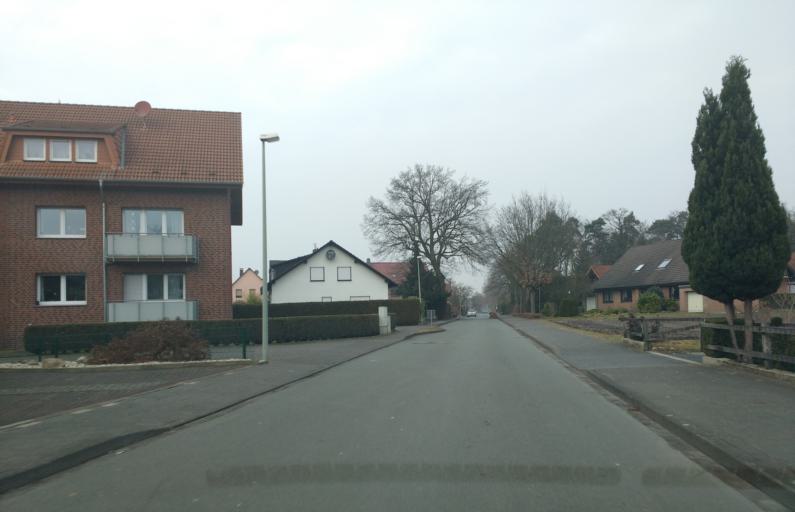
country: DE
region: North Rhine-Westphalia
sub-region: Regierungsbezirk Detmold
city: Paderborn
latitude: 51.7549
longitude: 8.7422
